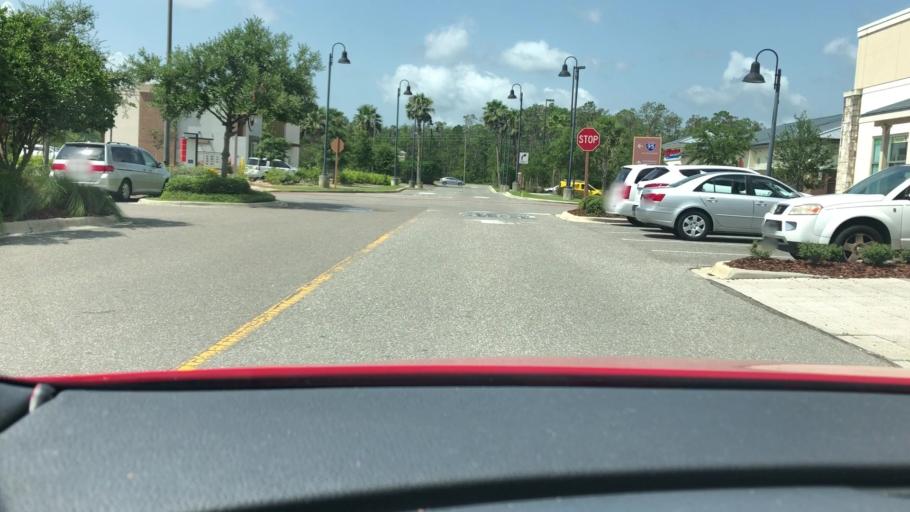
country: US
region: Florida
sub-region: Volusia County
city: Port Orange
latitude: 29.1107
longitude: -81.0362
